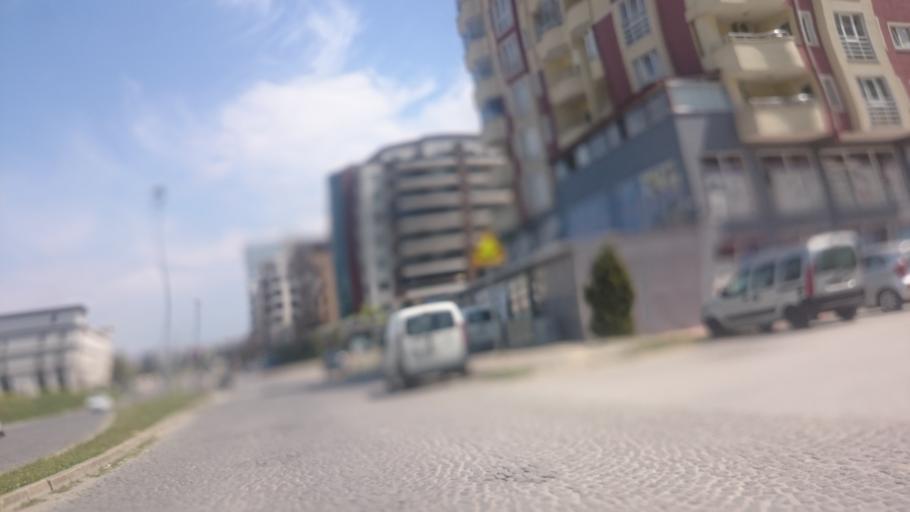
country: TR
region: Bursa
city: Cali
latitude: 40.2225
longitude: 28.9437
